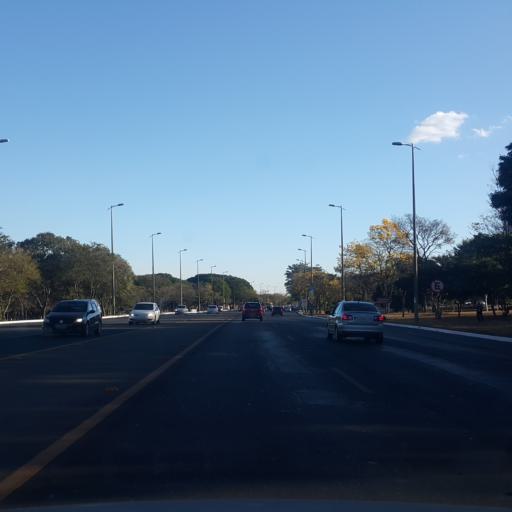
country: BR
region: Federal District
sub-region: Brasilia
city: Brasilia
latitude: -15.8019
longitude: -47.8862
